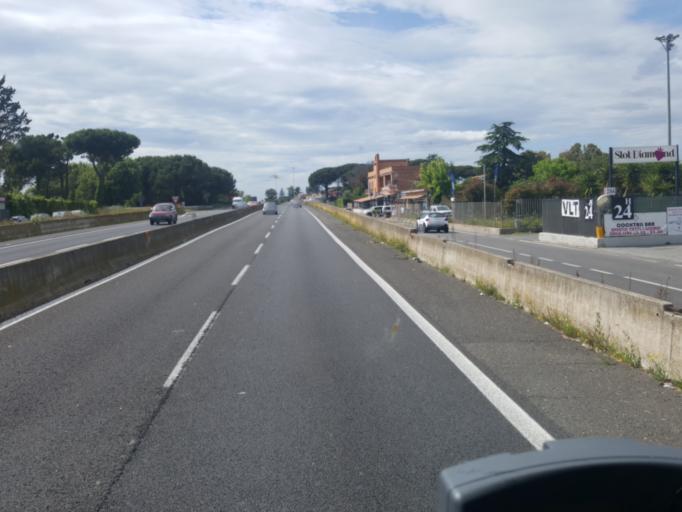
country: IT
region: Latium
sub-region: Citta metropolitana di Roma Capitale
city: Ara Nova
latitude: 41.9148
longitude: 12.2447
